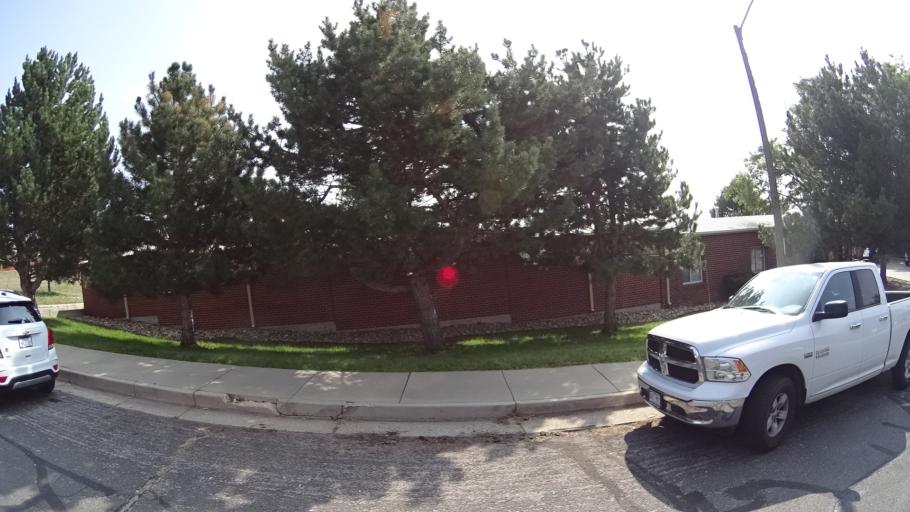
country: US
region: Colorado
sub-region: El Paso County
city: Colorado Springs
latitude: 38.8479
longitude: -104.7781
